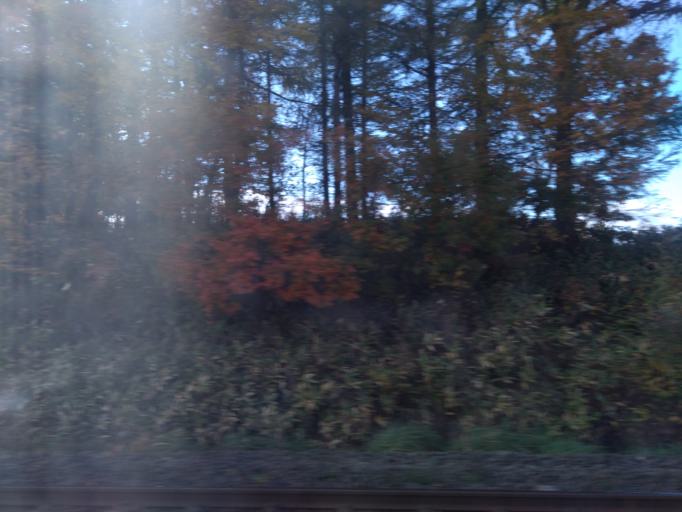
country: JP
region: Hokkaido
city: Kitahiroshima
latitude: 42.9315
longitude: 141.5725
